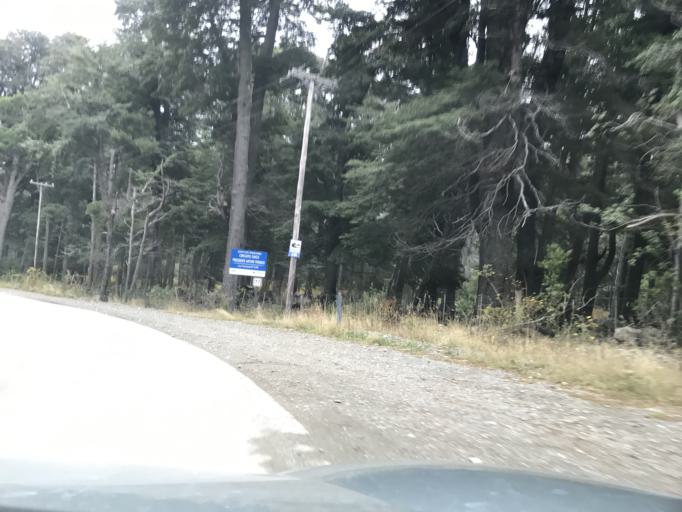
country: AR
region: Rio Negro
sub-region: Departamento de Bariloche
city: San Carlos de Bariloche
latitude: -41.0846
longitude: -71.5450
